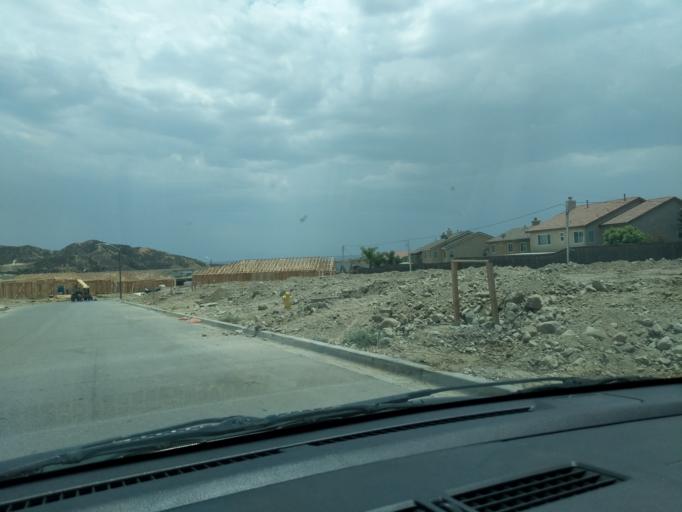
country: US
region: California
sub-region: San Bernardino County
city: Muscoy
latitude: 34.1856
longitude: -117.4079
